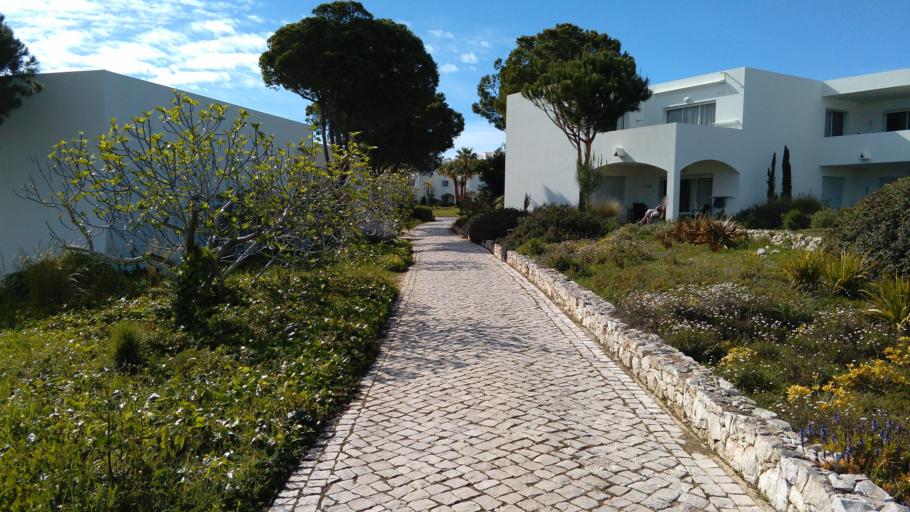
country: PT
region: Faro
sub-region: Albufeira
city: Albufeira
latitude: 37.0765
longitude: -8.2947
